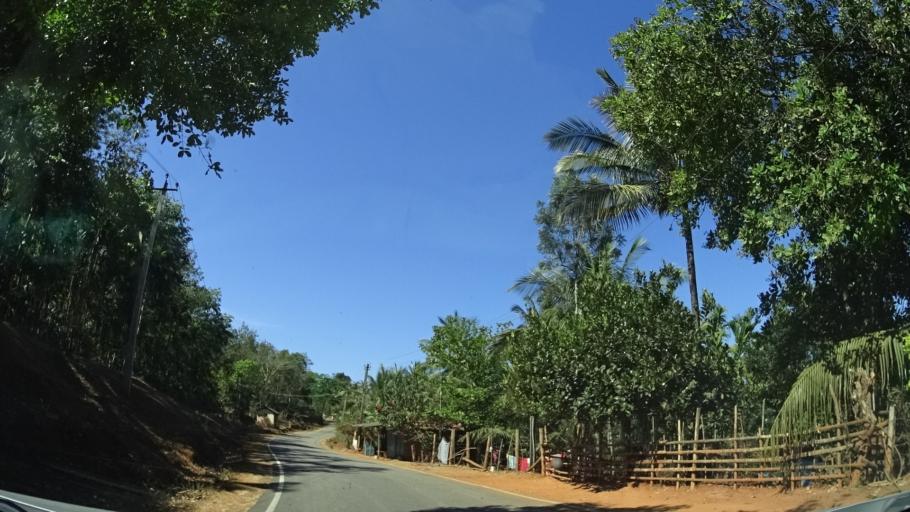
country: IN
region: Karnataka
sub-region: Chikmagalur
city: Sringeri
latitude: 13.2466
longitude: 75.3817
